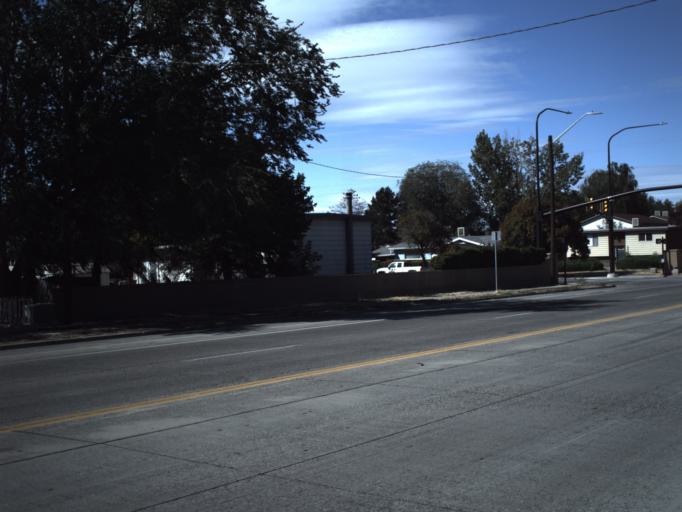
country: US
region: Utah
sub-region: Salt Lake County
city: Salt Lake City
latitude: 40.7755
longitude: -111.9392
